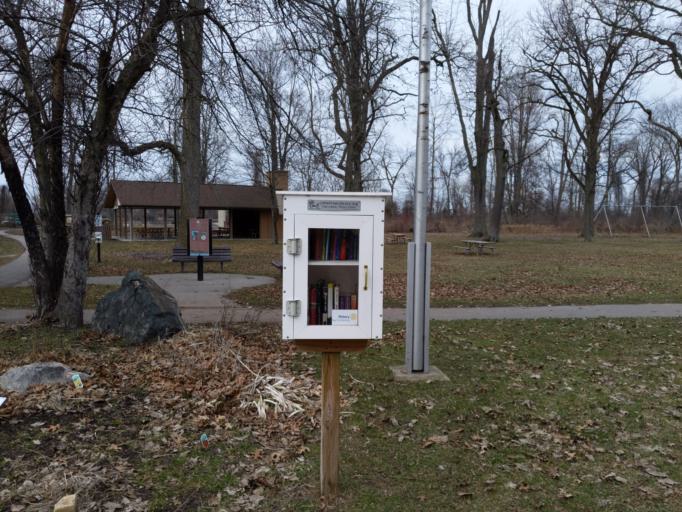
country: US
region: Michigan
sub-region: Bay County
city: Bay City
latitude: 43.6699
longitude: -83.9110
